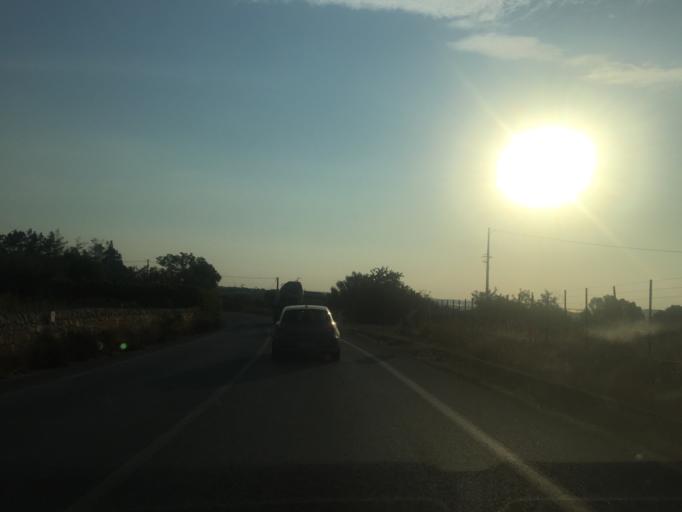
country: IT
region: Sicily
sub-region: Ragusa
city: Ispica
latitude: 36.7567
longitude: 14.8914
